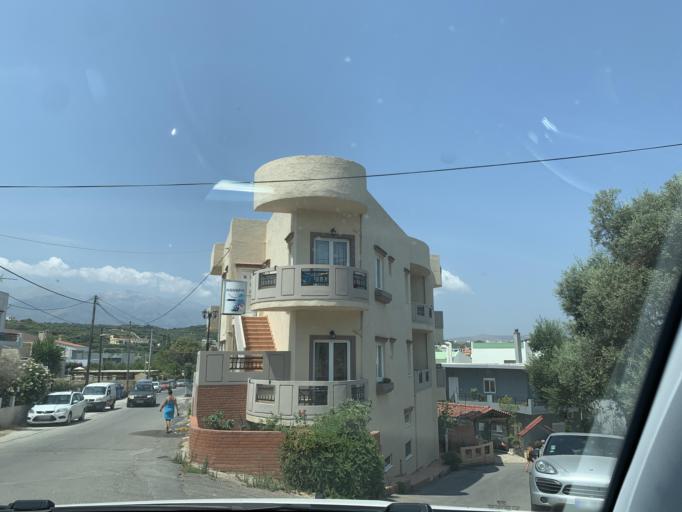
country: GR
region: Crete
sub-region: Nomos Chanias
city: Kalivai
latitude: 35.4488
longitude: 24.2037
